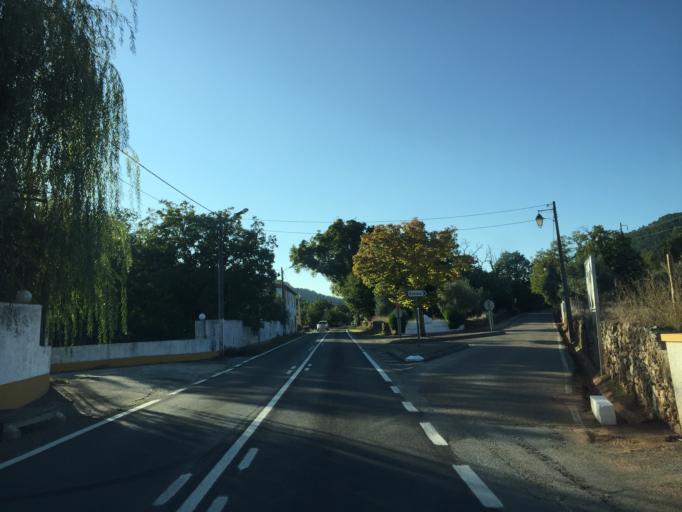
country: PT
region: Portalegre
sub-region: Marvao
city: Marvao
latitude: 39.3877
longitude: -7.4042
